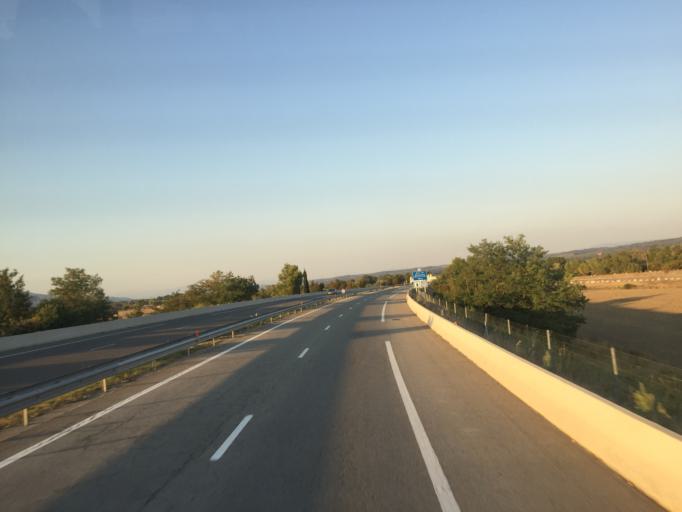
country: FR
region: Provence-Alpes-Cote d'Azur
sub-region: Departement des Alpes-de-Haute-Provence
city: Sainte-Tulle
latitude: 43.7661
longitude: 5.7824
